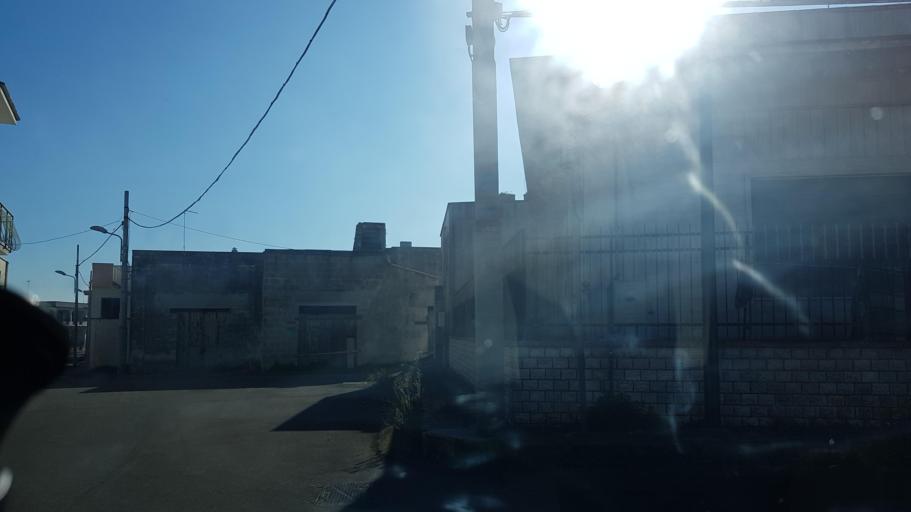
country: IT
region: Apulia
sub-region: Provincia di Lecce
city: Squinzano
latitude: 40.4317
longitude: 18.0456
